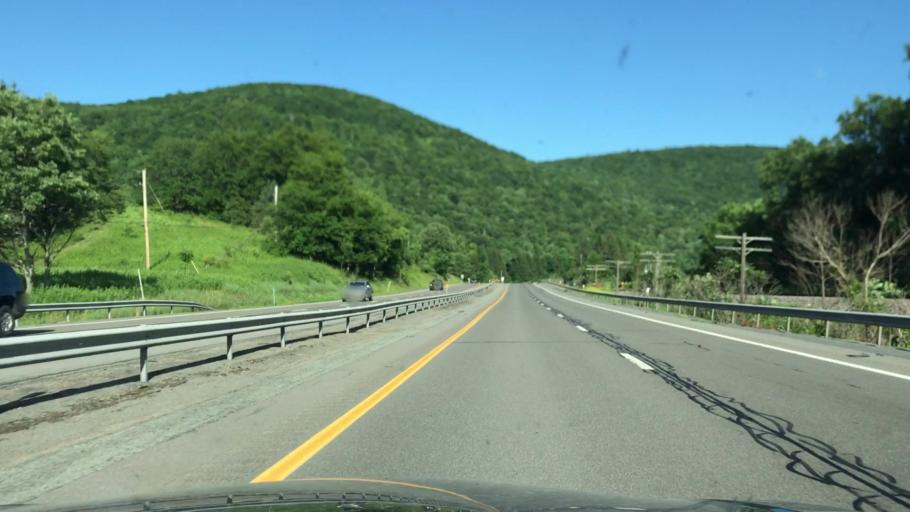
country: US
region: New York
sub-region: Delaware County
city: Hancock
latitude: 41.9972
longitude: -75.3488
